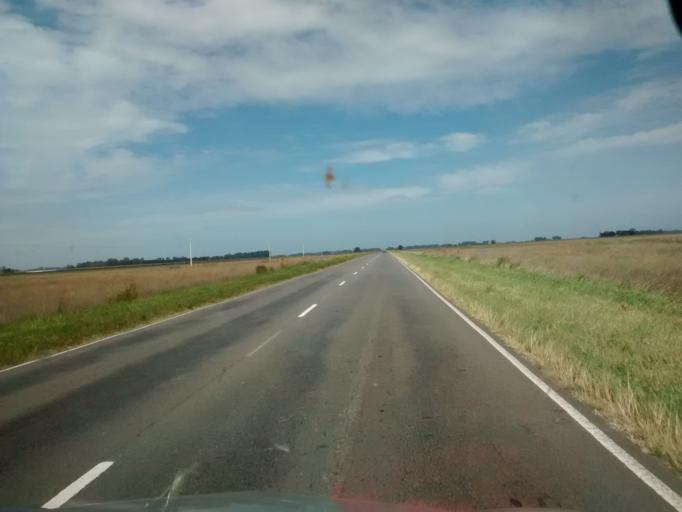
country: AR
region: Buenos Aires
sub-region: Partido de Ayacucho
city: Ayacucho
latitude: -37.0684
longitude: -58.5443
